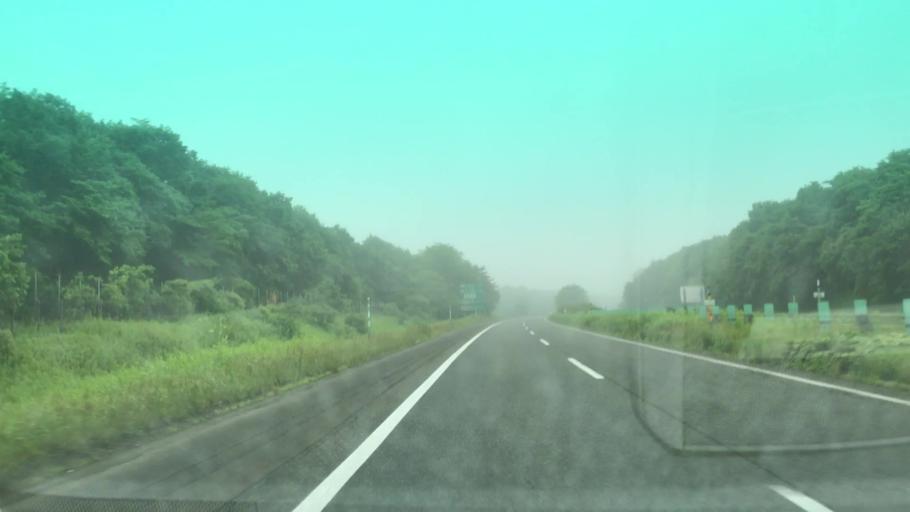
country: JP
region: Hokkaido
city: Chitose
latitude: 42.8013
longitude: 141.6255
